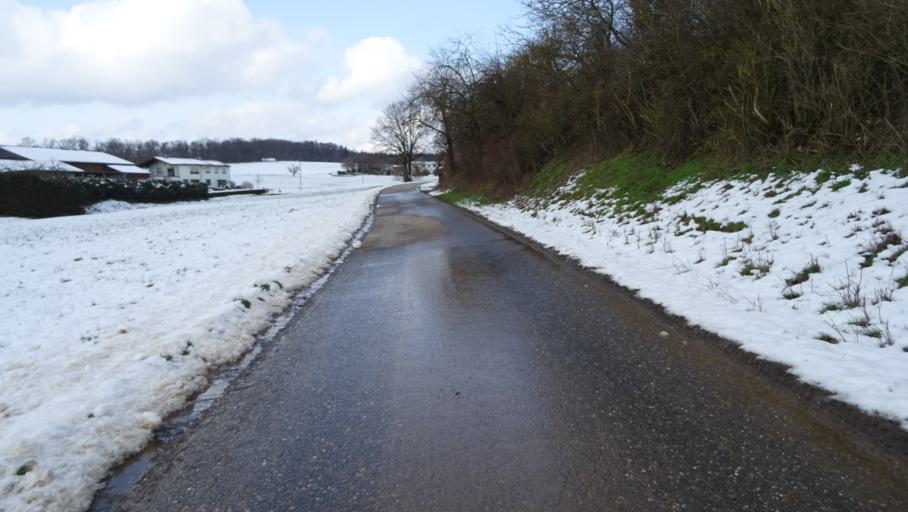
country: DE
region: Baden-Wuerttemberg
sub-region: Karlsruhe Region
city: Seckach
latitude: 49.4262
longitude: 9.2688
